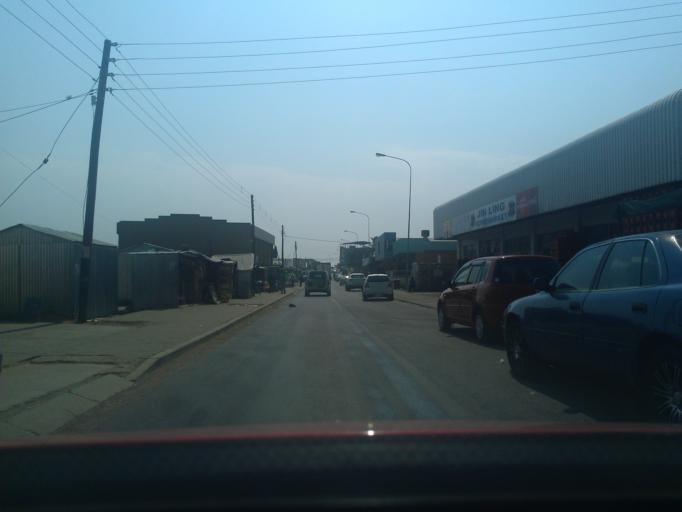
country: LS
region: Berea
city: Teyateyaneng
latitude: -29.1504
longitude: 27.7451
